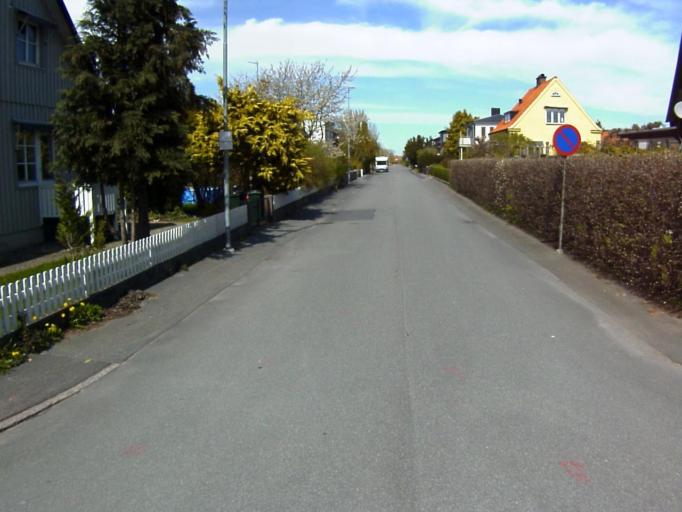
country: SE
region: Skane
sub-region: Kristianstads Kommun
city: Kristianstad
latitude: 56.0510
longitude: 14.1517
